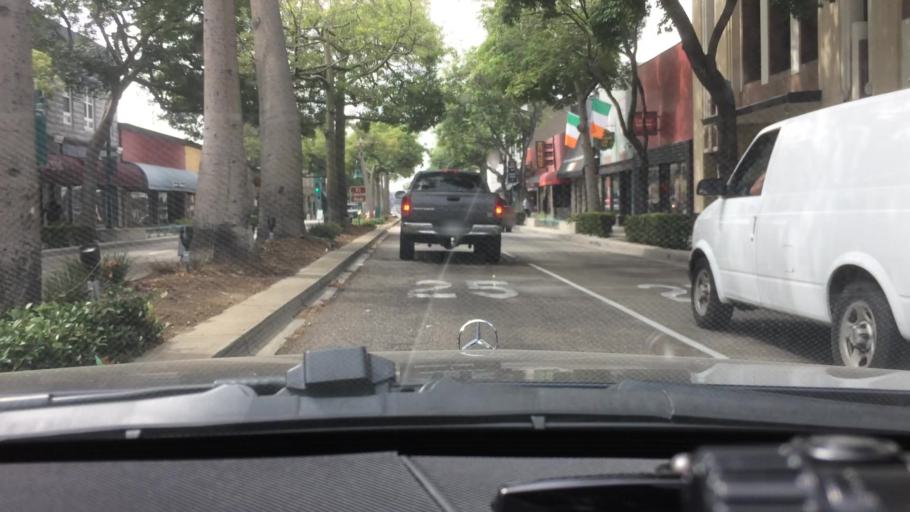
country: US
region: California
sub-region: Orange County
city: Fullerton
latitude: 33.8723
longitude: -117.9244
